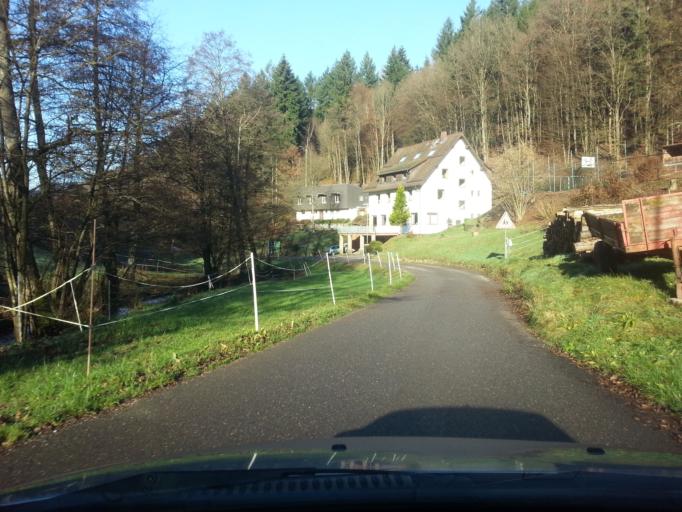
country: DE
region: Baden-Wuerttemberg
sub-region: Karlsruhe Region
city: Zwingenberg
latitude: 49.4834
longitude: 9.0619
